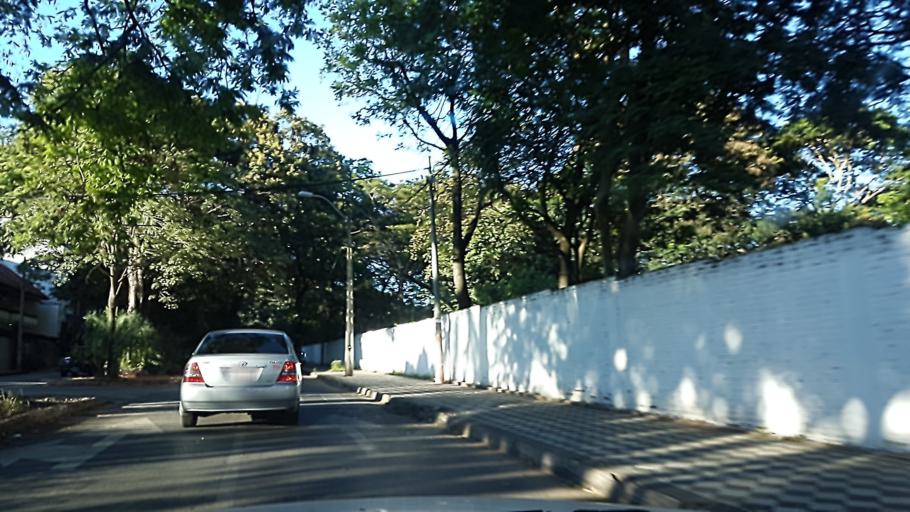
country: PY
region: Asuncion
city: Asuncion
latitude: -25.2734
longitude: -57.5767
